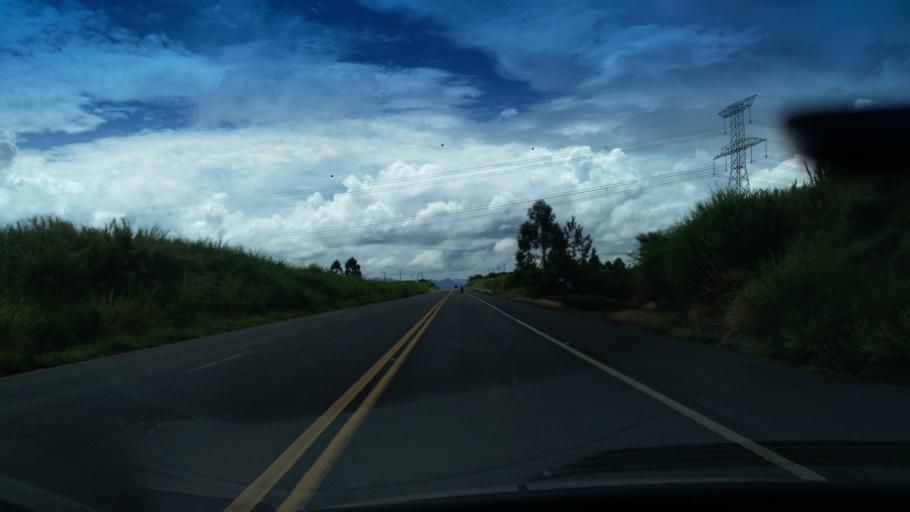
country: BR
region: Sao Paulo
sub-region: Santo Antonio Do Jardim
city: Espirito Santo do Pinhal
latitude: -22.1401
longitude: -46.7092
